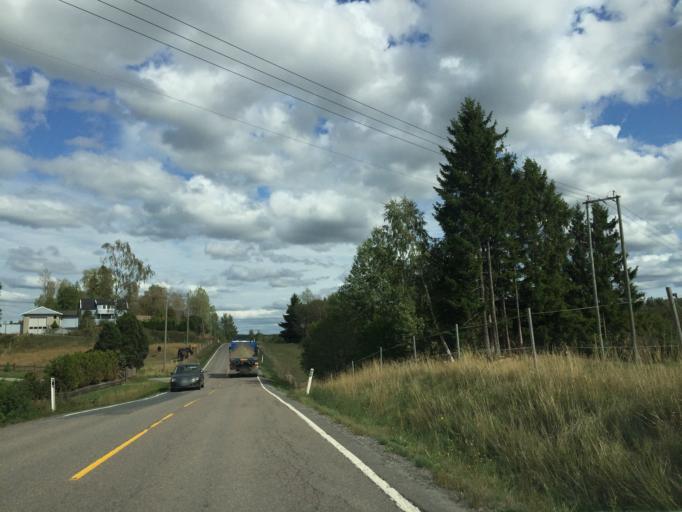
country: NO
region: Ostfold
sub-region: Hobol
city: Elvestad
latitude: 59.6078
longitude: 10.9176
